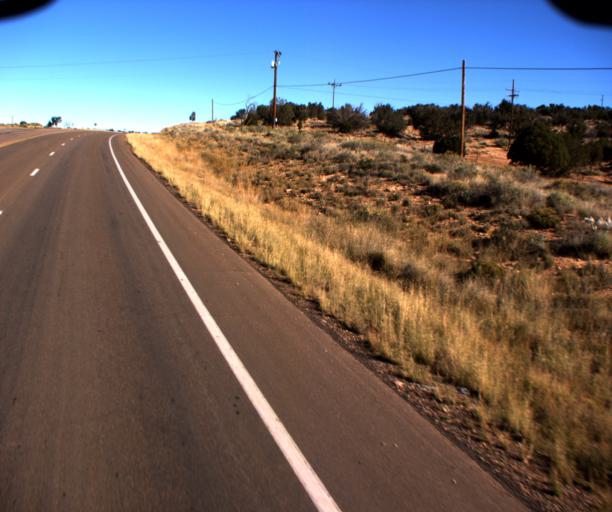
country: US
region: Arizona
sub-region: Navajo County
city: Snowflake
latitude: 34.5297
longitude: -110.0815
